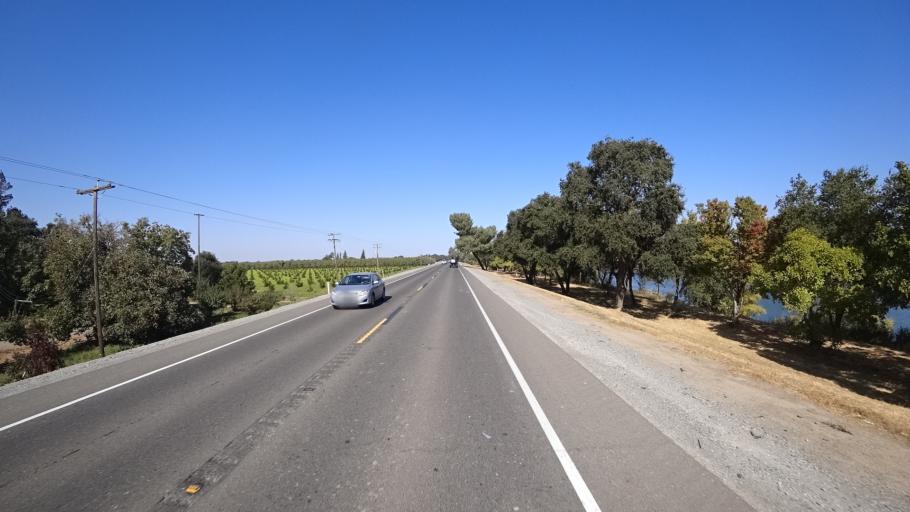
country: US
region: California
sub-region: Yolo County
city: West Sacramento
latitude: 38.6250
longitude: -121.5636
